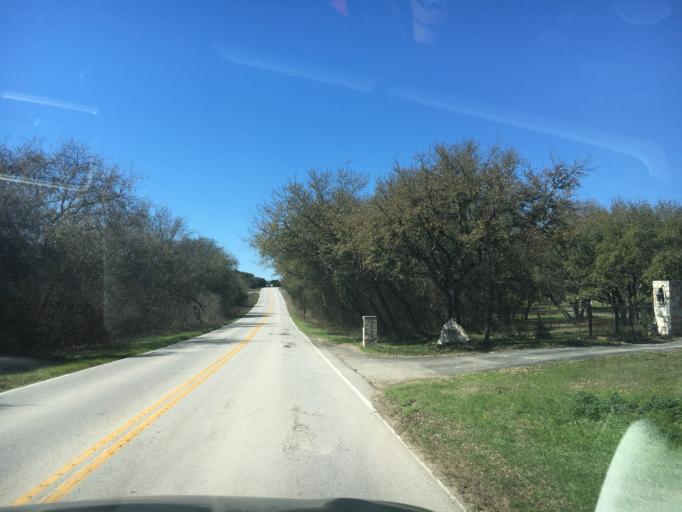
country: US
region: Texas
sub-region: Hays County
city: Dripping Springs
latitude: 30.2922
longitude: -98.0803
